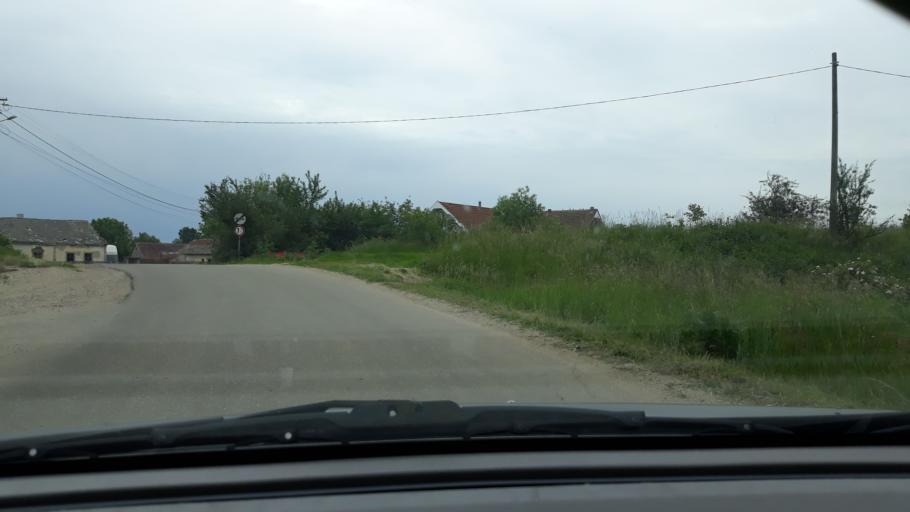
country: RO
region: Bihor
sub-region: Comuna Osorheiu
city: Osorheiu
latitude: 47.0642
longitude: 22.0414
